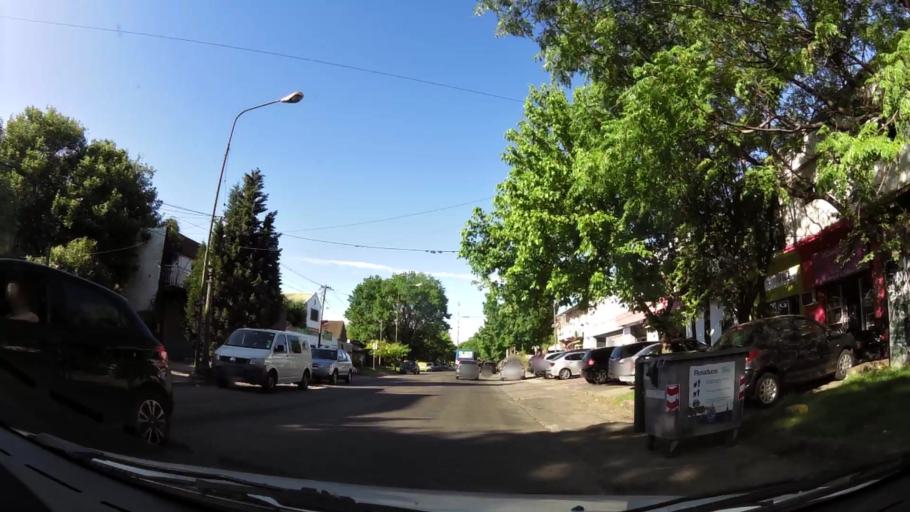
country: AR
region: Buenos Aires
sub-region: Partido de San Isidro
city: San Isidro
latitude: -34.4636
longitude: -58.5096
